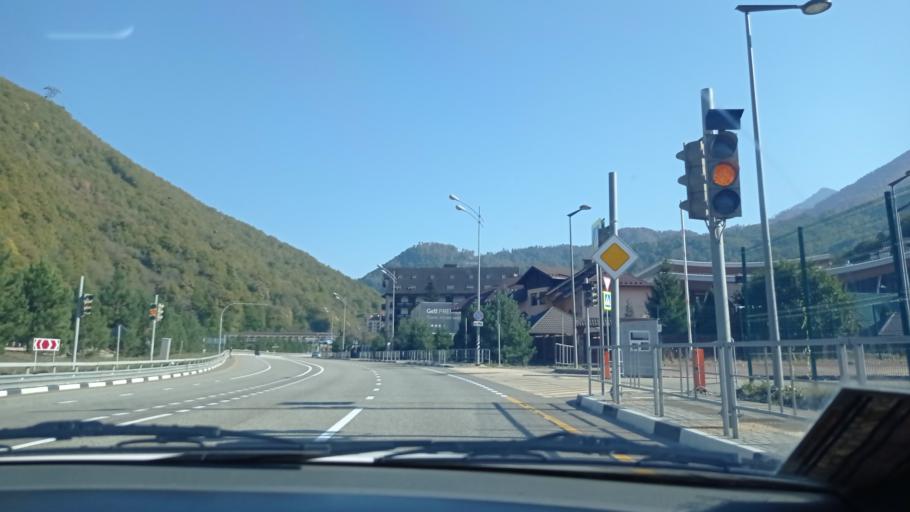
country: RU
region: Krasnodarskiy
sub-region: Sochi City
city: Krasnaya Polyana
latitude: 43.6787
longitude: 40.2787
